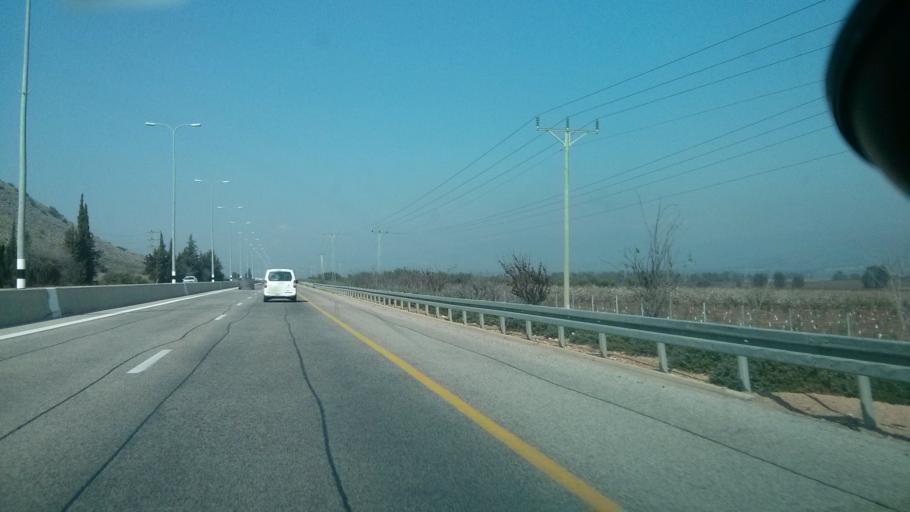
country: IL
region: Northern District
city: Rosh Pinna
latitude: 33.0621
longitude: 35.5747
